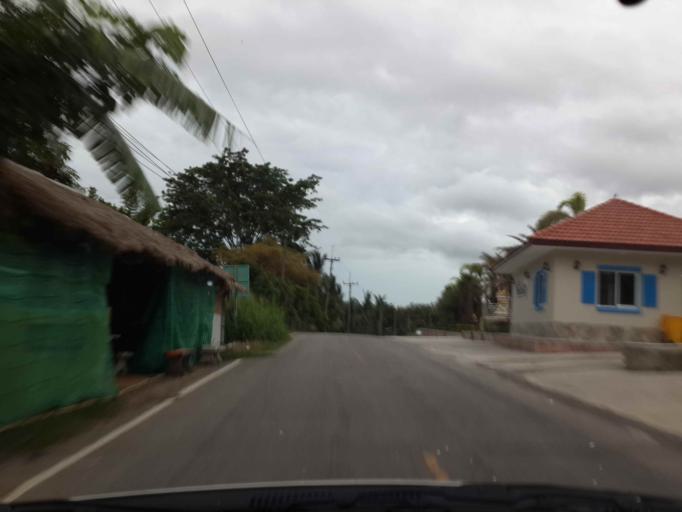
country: TH
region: Ratchaburi
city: Suan Phueng
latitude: 13.5884
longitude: 99.2101
